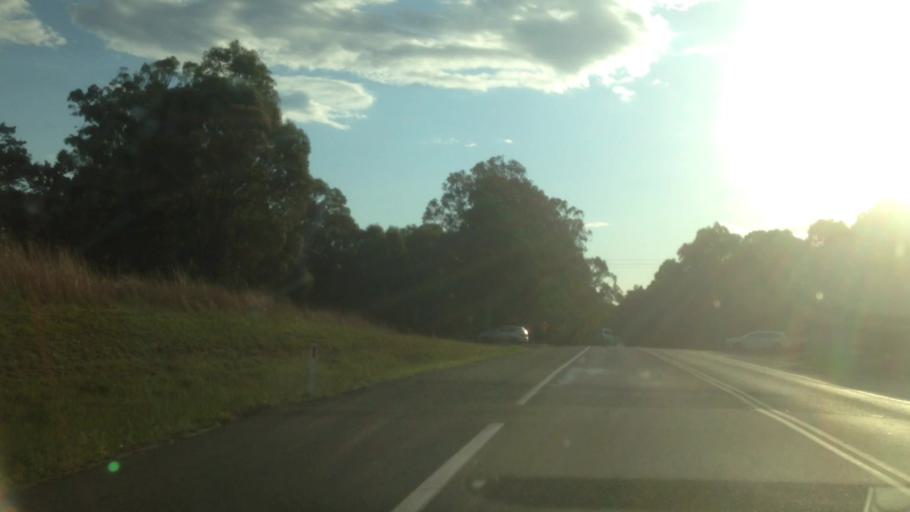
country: AU
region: New South Wales
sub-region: Cessnock
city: Heddon Greta
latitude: -32.8300
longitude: 151.5142
